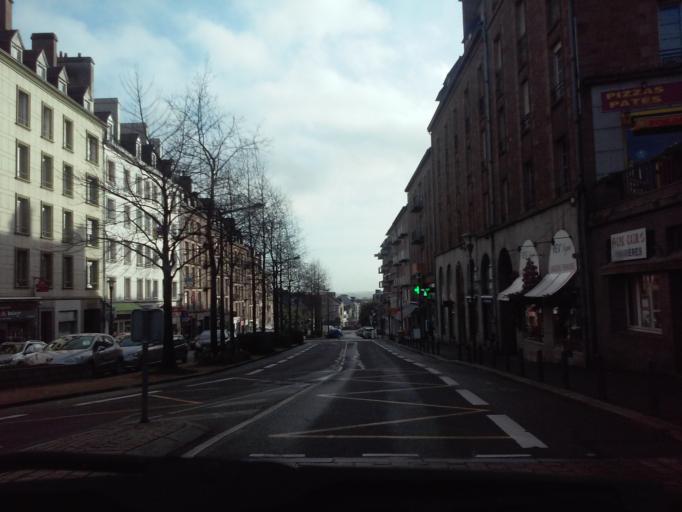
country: FR
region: Brittany
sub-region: Departement d'Ille-et-Vilaine
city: Fougeres
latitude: 48.3547
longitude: -1.2009
